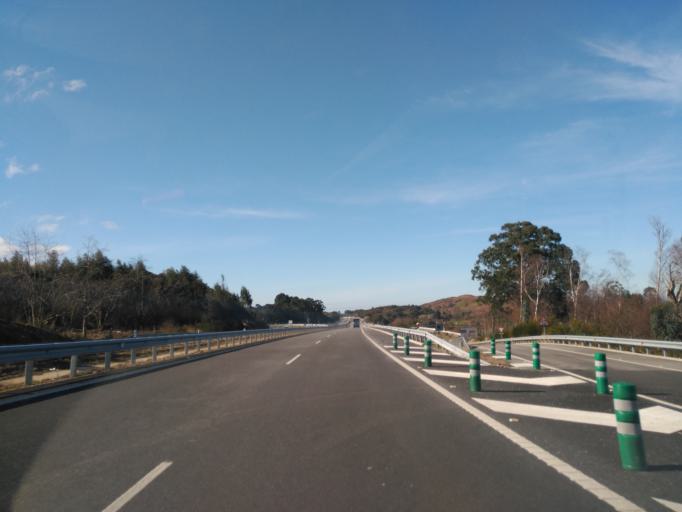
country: ES
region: Asturias
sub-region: Province of Asturias
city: Llanes
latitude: 43.3946
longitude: -4.6501
